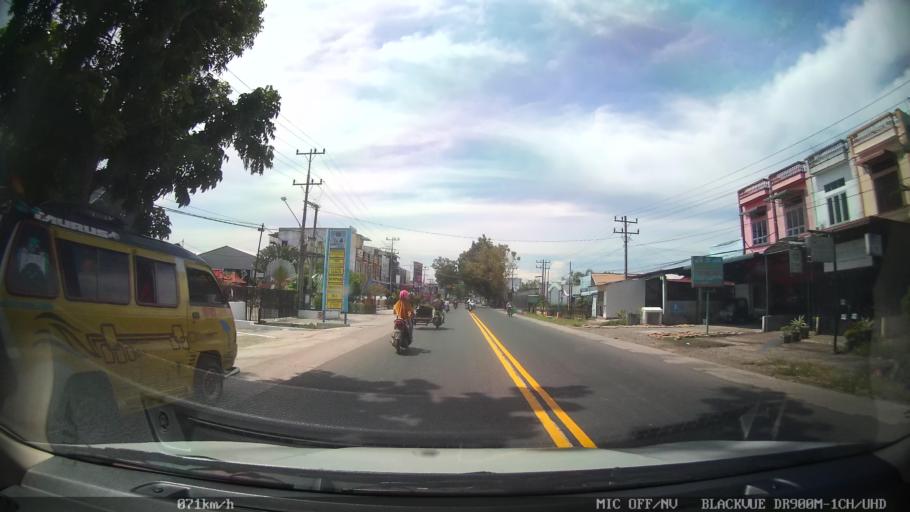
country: ID
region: North Sumatra
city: Binjai
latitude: 3.6468
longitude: 98.5102
